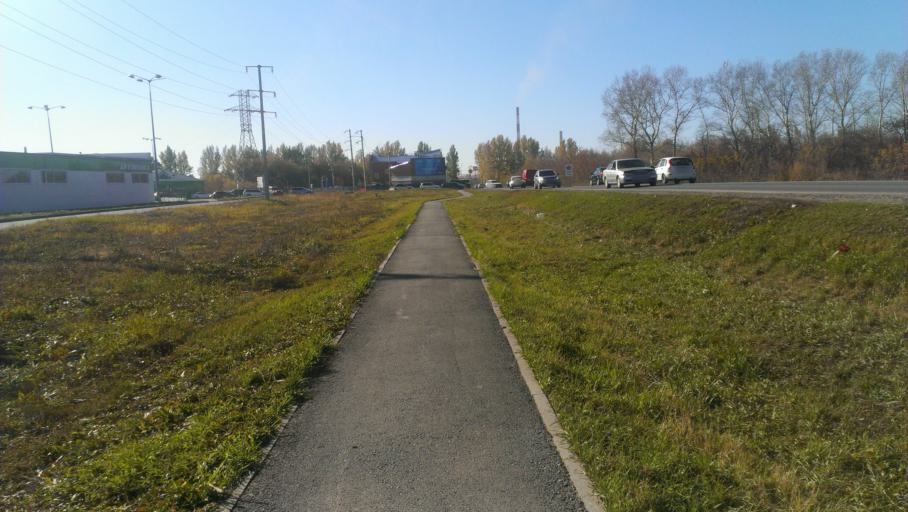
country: RU
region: Altai Krai
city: Novosilikatnyy
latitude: 53.3510
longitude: 83.6310
